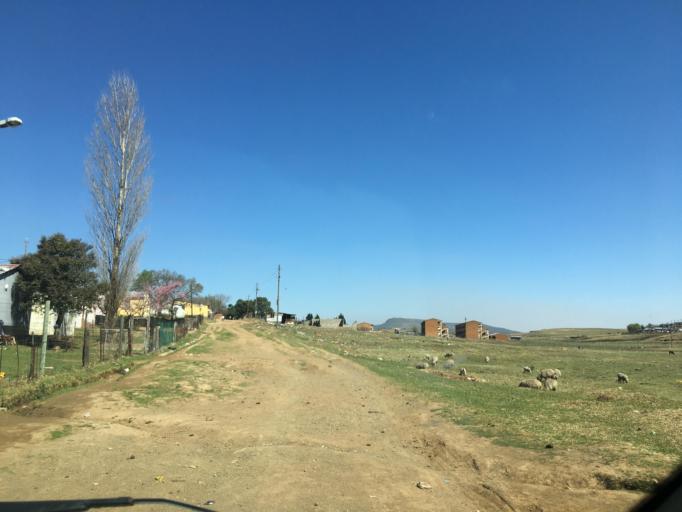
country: ZA
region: Eastern Cape
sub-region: Chris Hani District Municipality
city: Elliot
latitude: -31.3271
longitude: 27.8256
